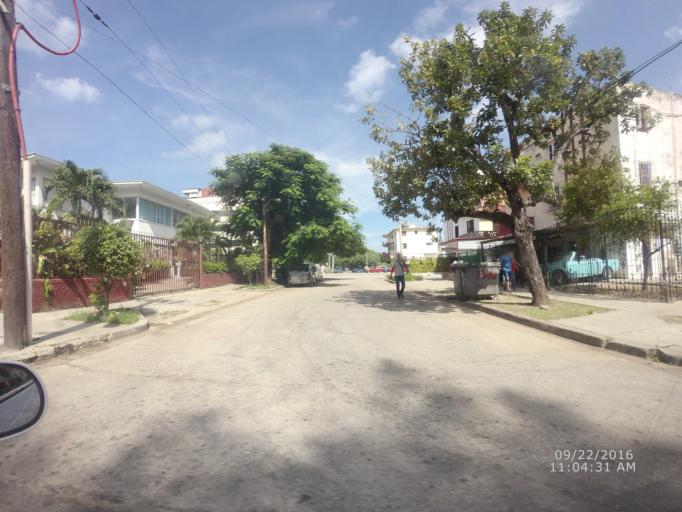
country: CU
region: La Habana
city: Havana
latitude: 23.1253
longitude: -82.4134
